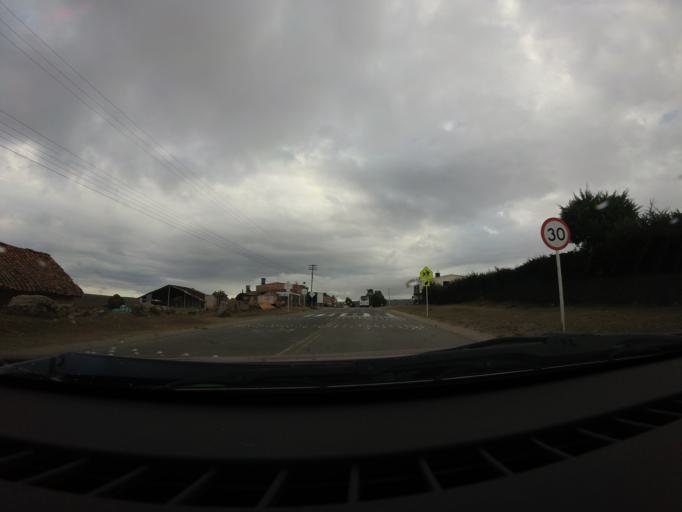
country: CO
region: Boyaca
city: Tunja
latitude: 5.5472
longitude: -73.4018
